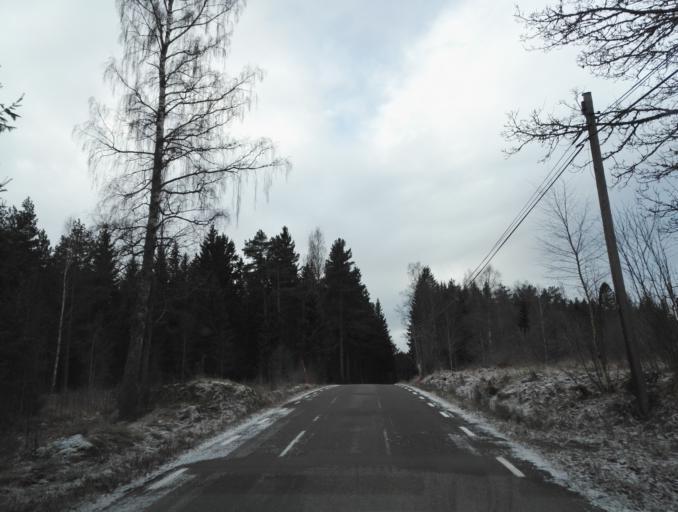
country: SE
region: Kalmar
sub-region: Hultsfreds Kommun
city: Malilla
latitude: 57.4663
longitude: 15.6619
